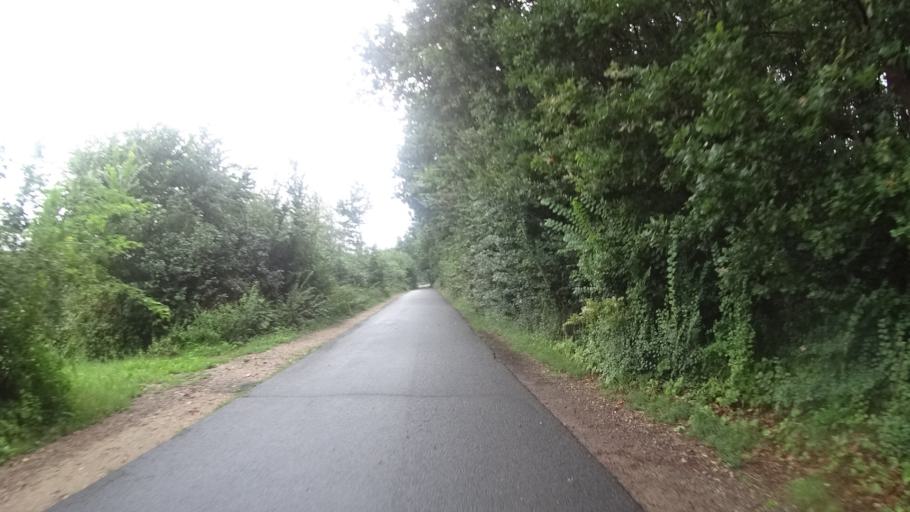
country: DE
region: Schleswig-Holstein
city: Siebeneichen
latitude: 53.5154
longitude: 10.6226
